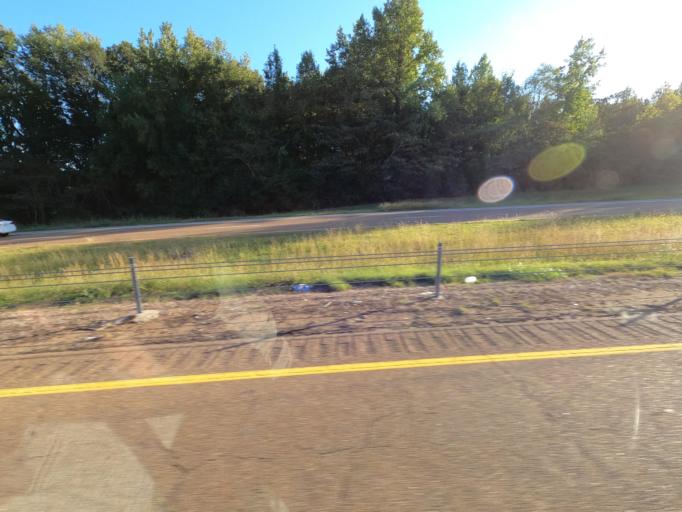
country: US
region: Tennessee
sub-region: Shelby County
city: Lakeland
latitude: 35.3077
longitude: -89.8000
